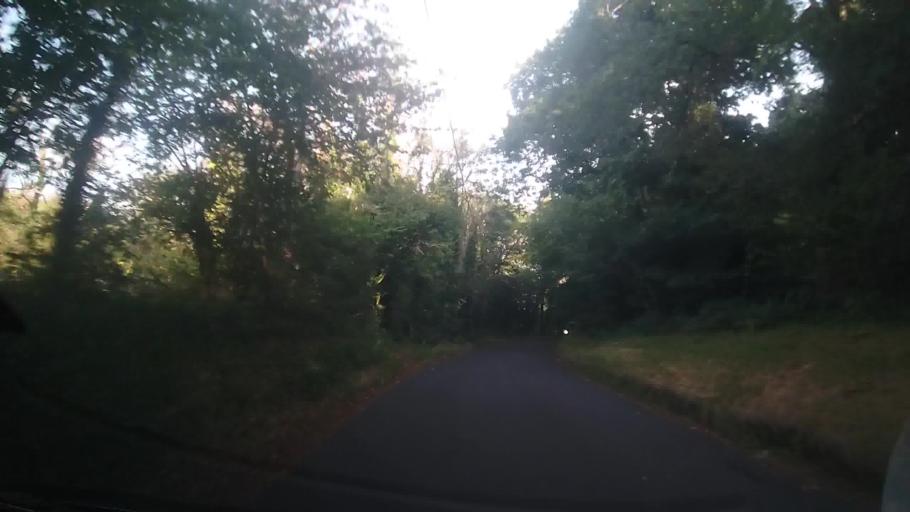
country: GB
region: Wales
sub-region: Pembrokeshire
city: Fishguard
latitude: 51.9826
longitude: -4.9388
